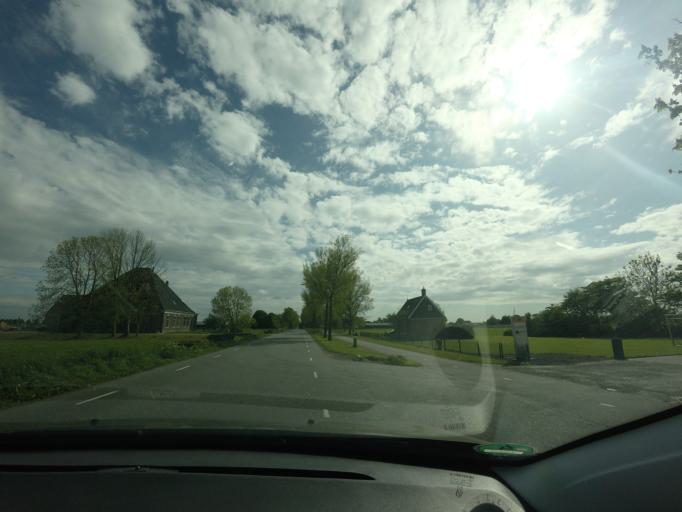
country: NL
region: North Holland
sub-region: Gemeente Beemster
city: Halfweg
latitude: 52.5667
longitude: 4.9240
